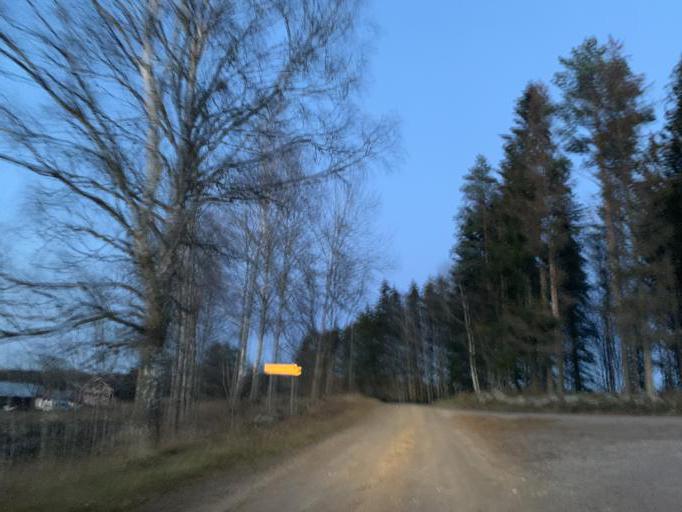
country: SE
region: OErebro
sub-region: Lindesbergs Kommun
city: Fellingsbro
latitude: 59.3626
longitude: 15.5934
